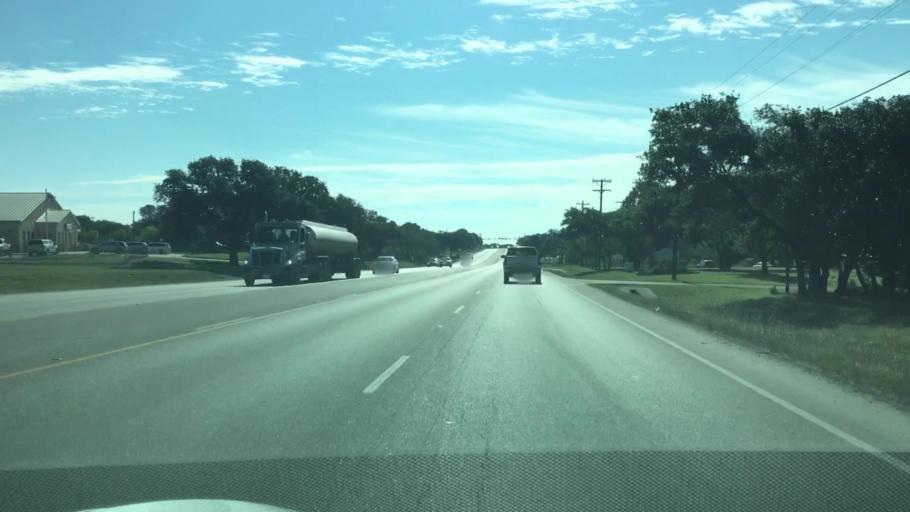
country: US
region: Texas
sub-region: Hays County
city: Dripping Springs
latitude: 30.2003
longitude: -98.1096
